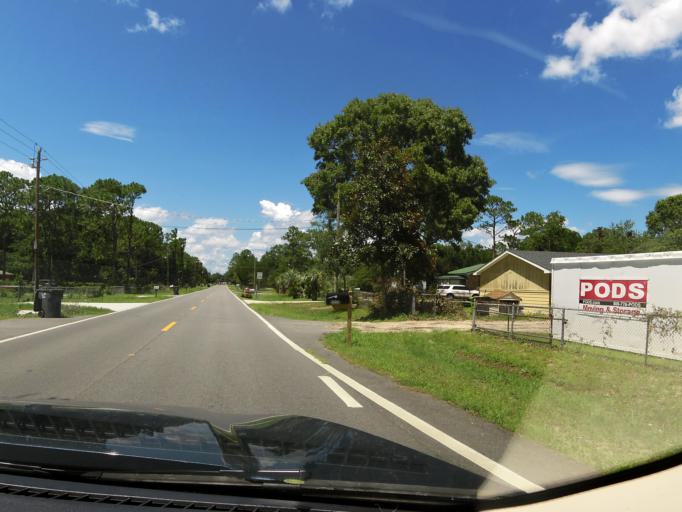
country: US
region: Georgia
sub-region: Camden County
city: St. Marys
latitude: 30.6690
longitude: -81.5408
